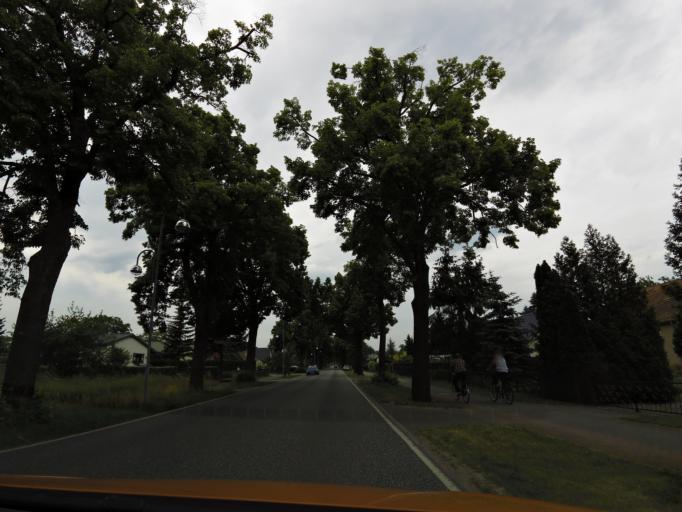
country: DE
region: Brandenburg
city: Zossen
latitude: 52.2073
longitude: 13.4554
